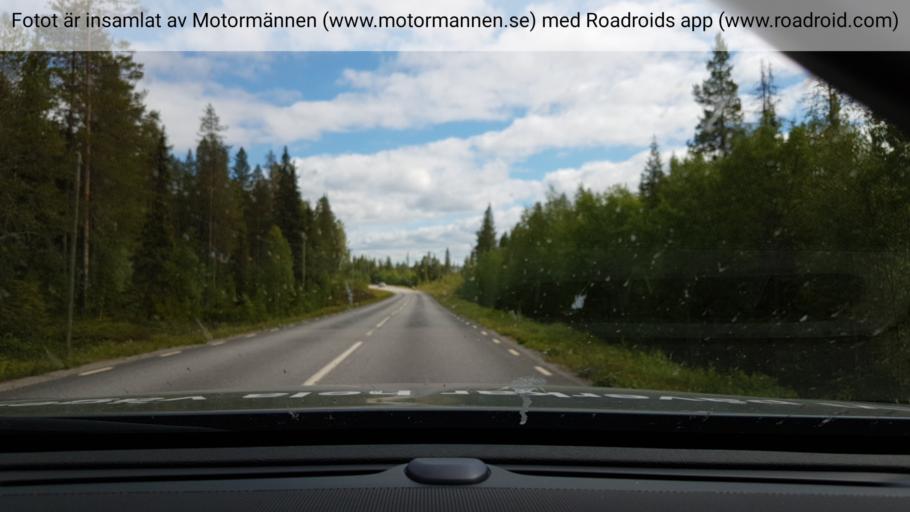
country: SE
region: Vaesterbotten
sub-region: Sorsele Kommun
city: Sorsele
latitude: 65.7021
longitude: 17.1594
